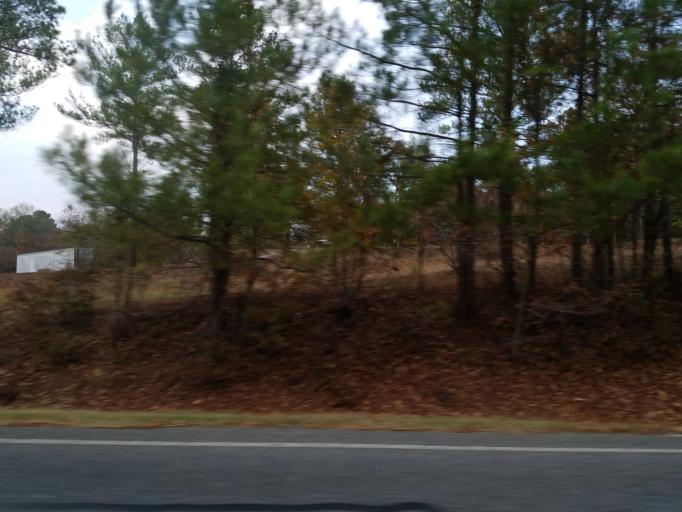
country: US
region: Georgia
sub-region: Murray County
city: Chatsworth
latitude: 34.6015
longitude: -84.7886
